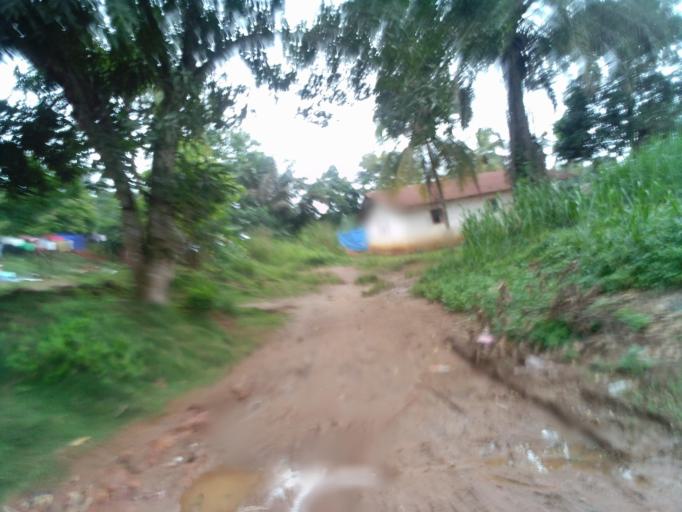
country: SL
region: Eastern Province
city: Kenema
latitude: 7.8528
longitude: -11.1866
